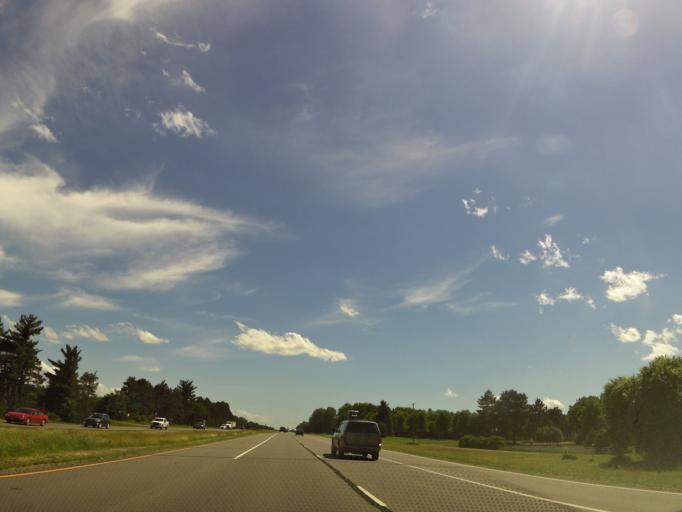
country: US
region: Minnesota
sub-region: Stearns County
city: Sartell
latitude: 45.6865
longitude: -94.1727
